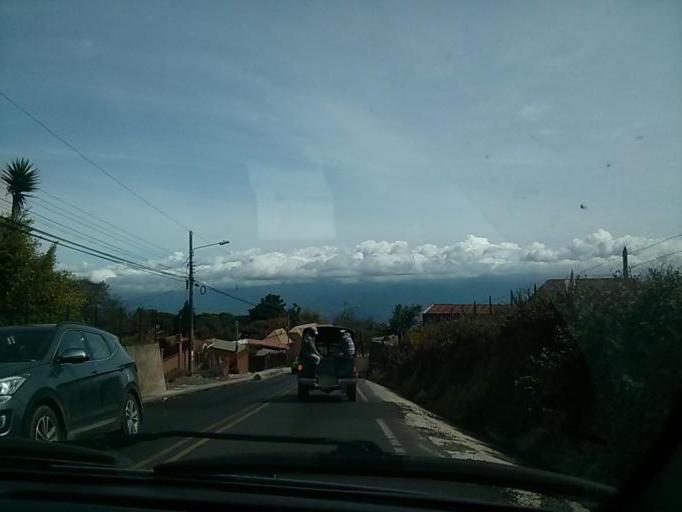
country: CR
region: Cartago
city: Cot
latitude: 9.9208
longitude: -83.8792
